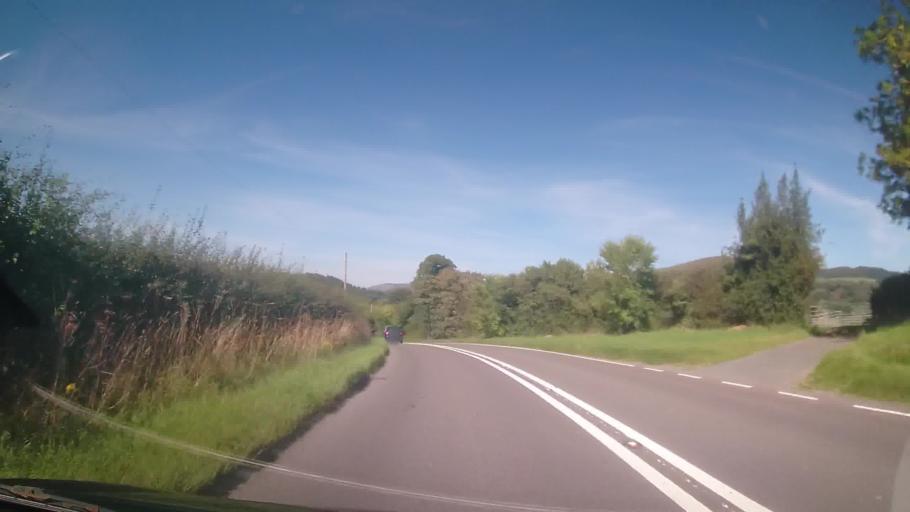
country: GB
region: England
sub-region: Shropshire
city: Lydham
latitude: 52.5179
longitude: -2.9826
